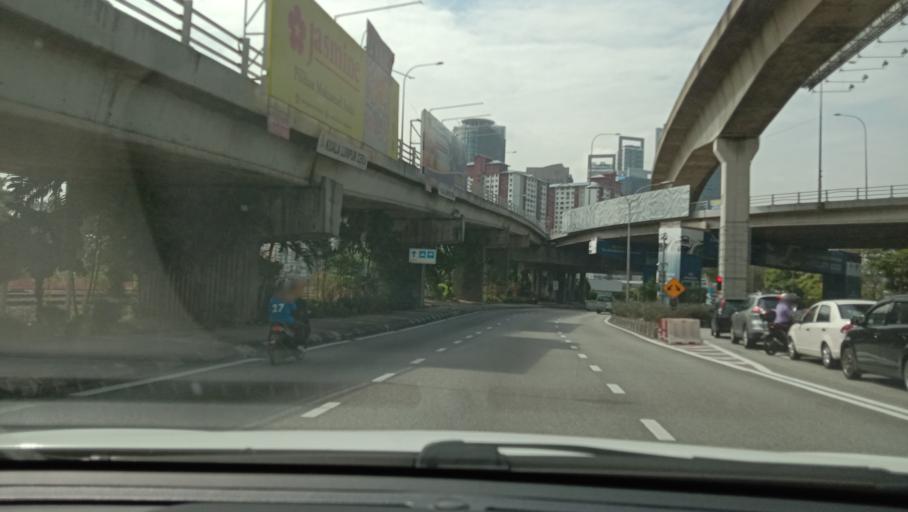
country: MY
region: Kuala Lumpur
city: Kuala Lumpur
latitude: 3.1259
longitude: 101.6783
